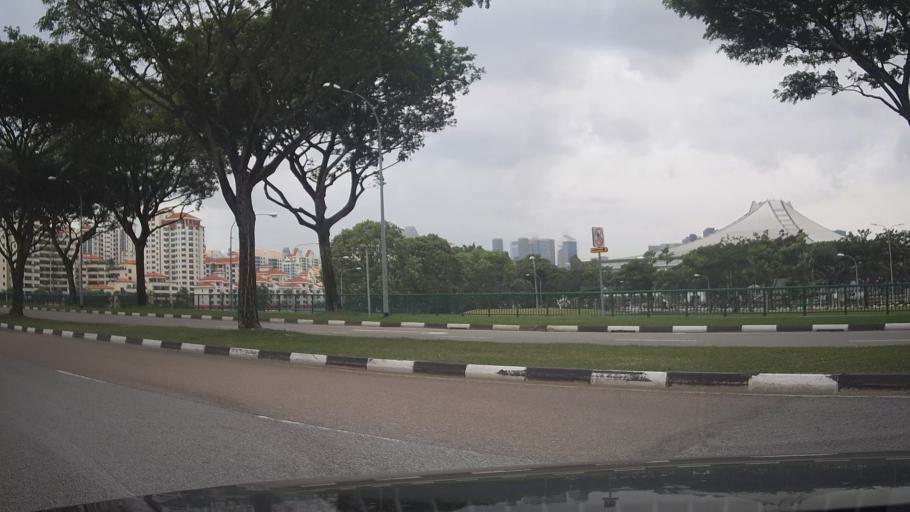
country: SG
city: Singapore
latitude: 1.3005
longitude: 103.8781
